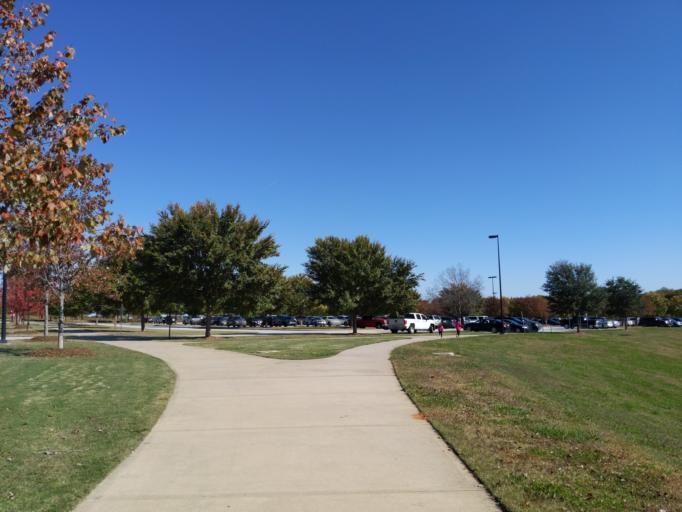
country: US
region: South Carolina
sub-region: Spartanburg County
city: Duncan
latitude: 34.8722
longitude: -82.1027
